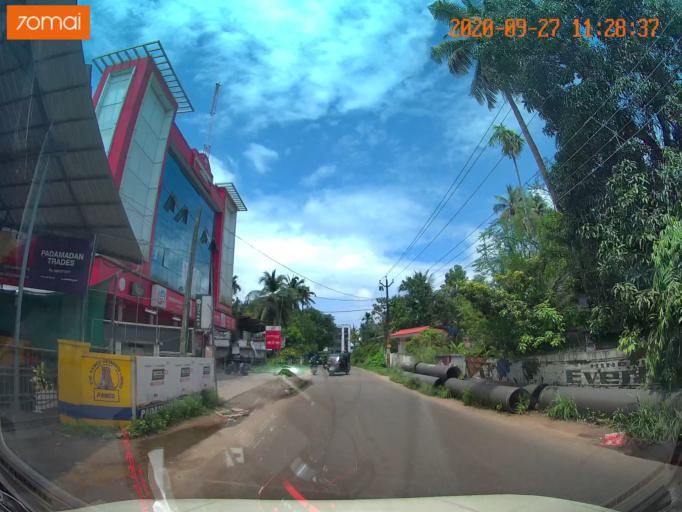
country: IN
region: Kerala
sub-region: Thrissur District
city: Thanniyam
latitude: 10.4162
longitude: 76.1378
